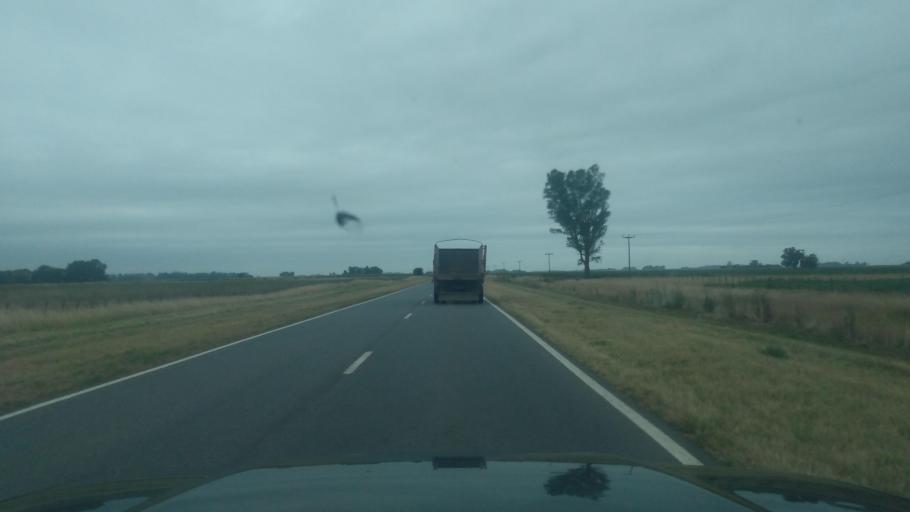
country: AR
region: Buenos Aires
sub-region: Partido de Nueve de Julio
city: Nueve de Julio
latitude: -35.3916
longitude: -60.7388
